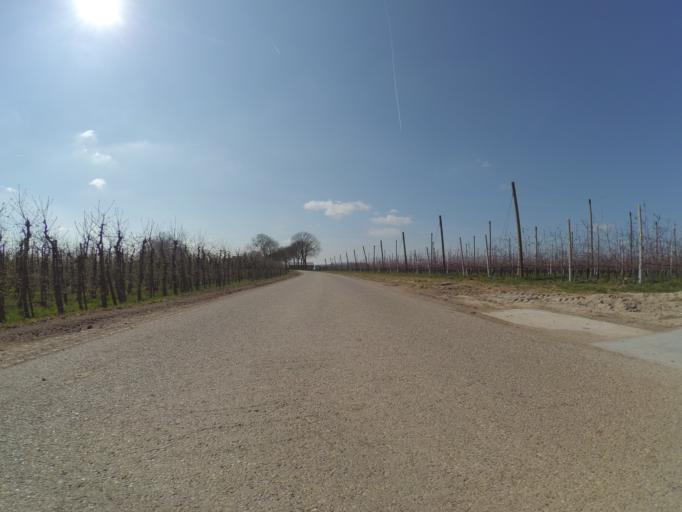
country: NL
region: Utrecht
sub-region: Gemeente Utrechtse Heuvelrug
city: Driebergen-Rijsenburg
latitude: 52.0072
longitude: 5.2754
